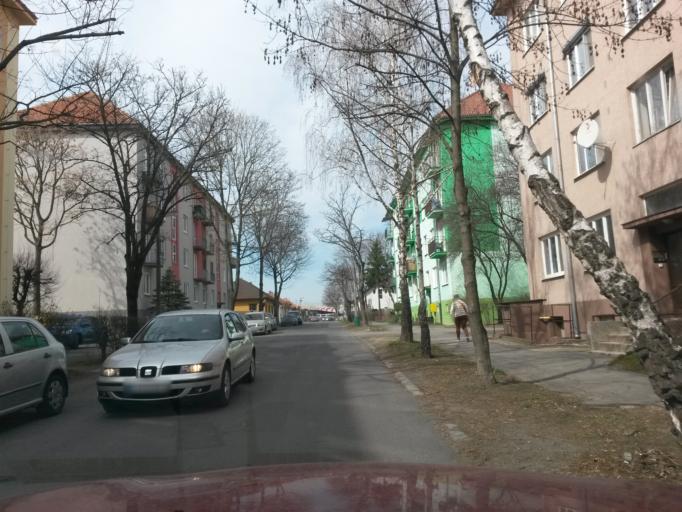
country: SK
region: Banskobystricky
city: Lucenec
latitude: 48.3357
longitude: 19.6641
